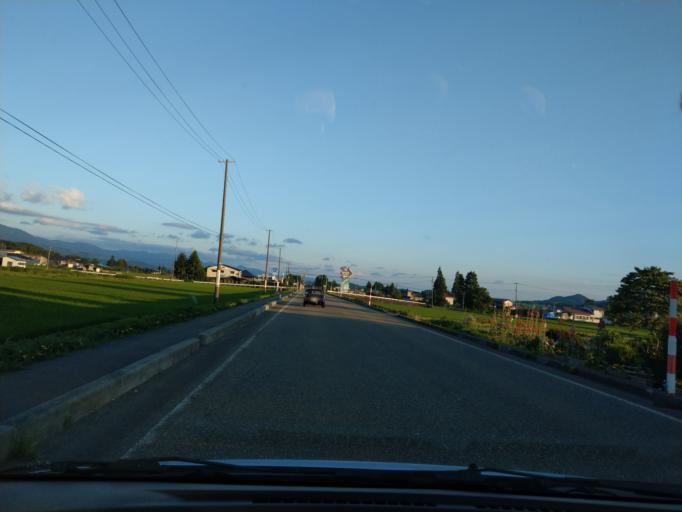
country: JP
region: Akita
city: Kakunodatemachi
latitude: 39.6616
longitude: 140.5696
